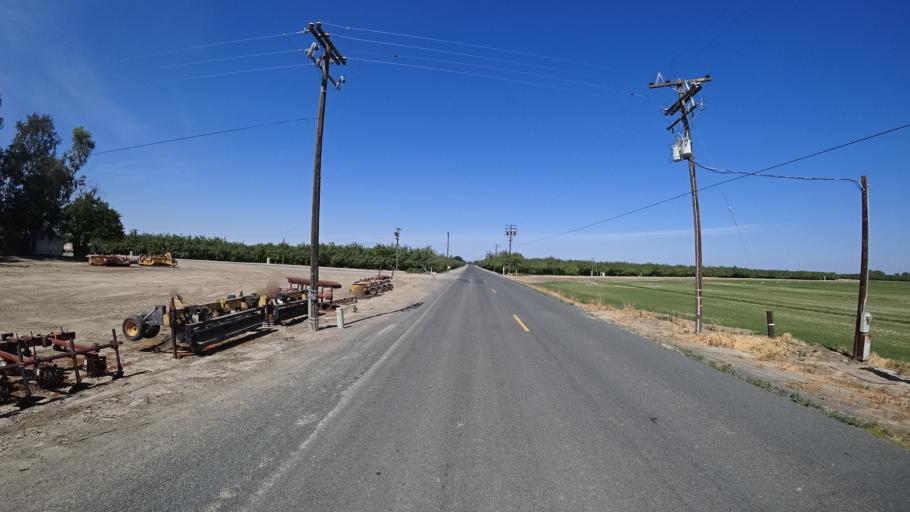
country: US
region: California
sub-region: Kings County
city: Armona
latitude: 36.2692
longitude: -119.7296
